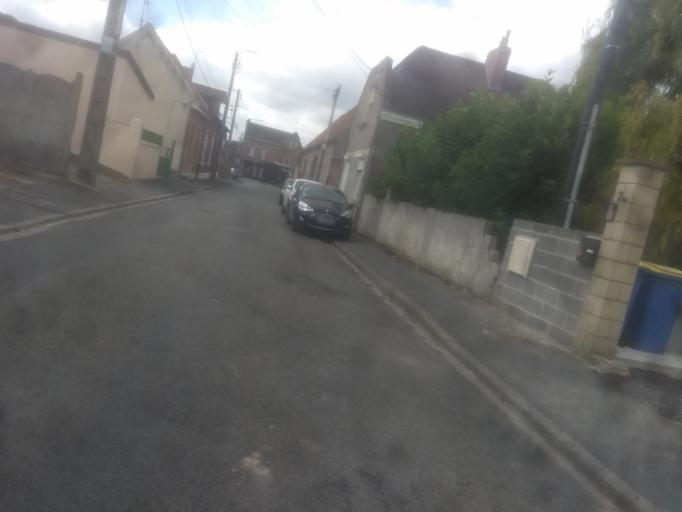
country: FR
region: Nord-Pas-de-Calais
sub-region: Departement du Pas-de-Calais
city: Agny
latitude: 50.2608
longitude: 2.7612
